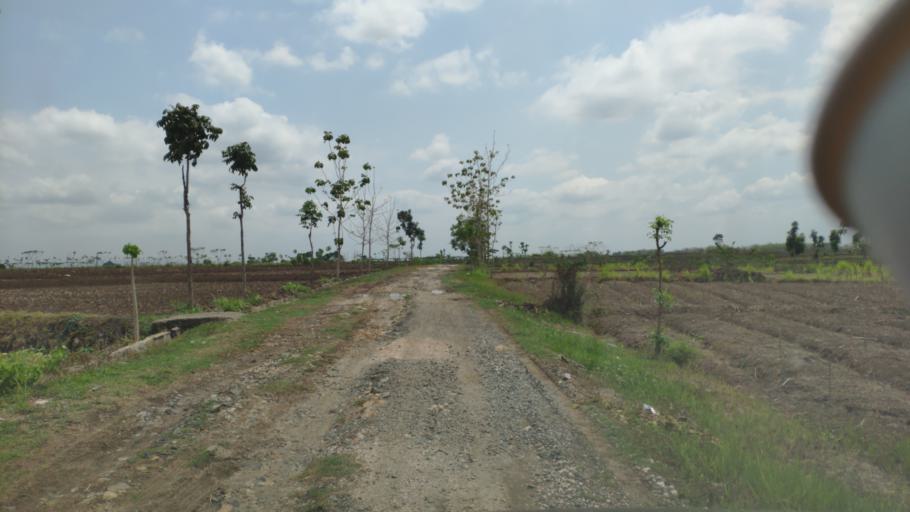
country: ID
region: Central Java
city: Gumiring
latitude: -7.0292
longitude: 111.3775
